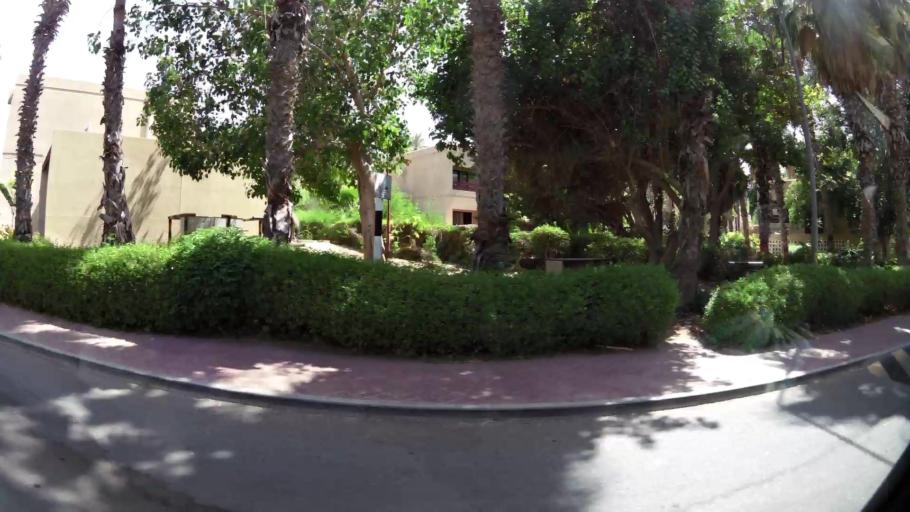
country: OM
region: Muhafazat Masqat
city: Muscat
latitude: 23.6329
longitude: 58.4926
